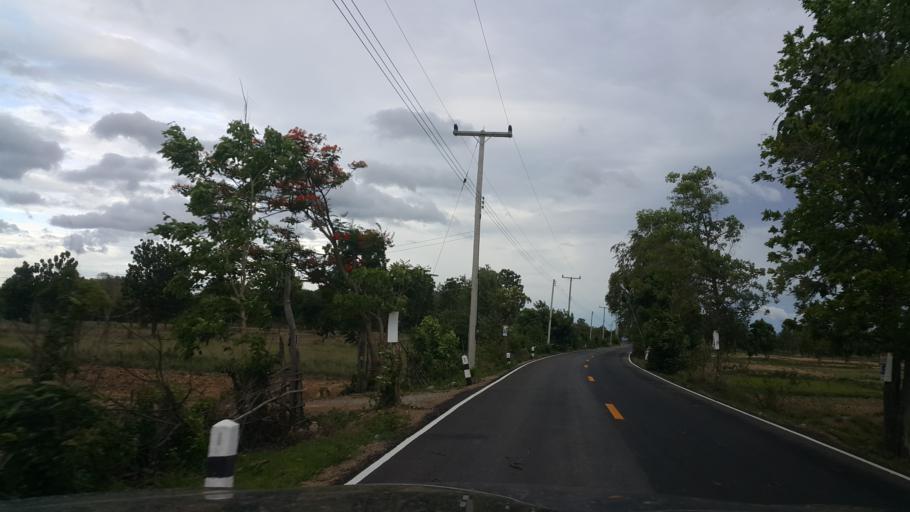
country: TH
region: Sukhothai
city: Thung Saliam
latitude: 17.1730
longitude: 99.4857
